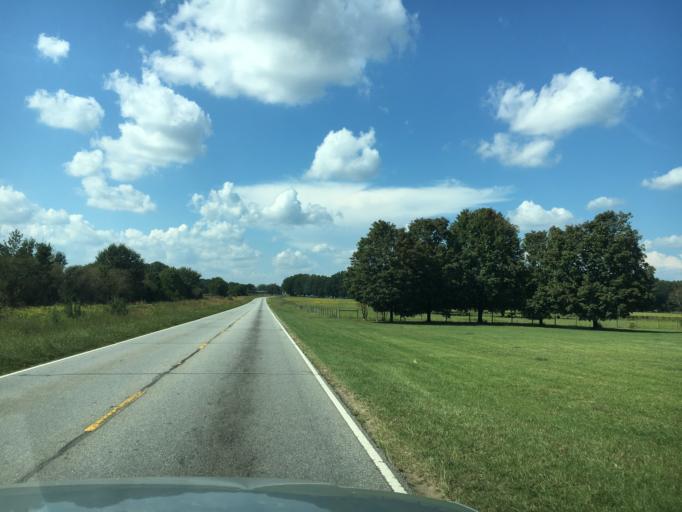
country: US
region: South Carolina
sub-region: Greenville County
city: Fountain Inn
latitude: 34.6232
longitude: -82.1271
